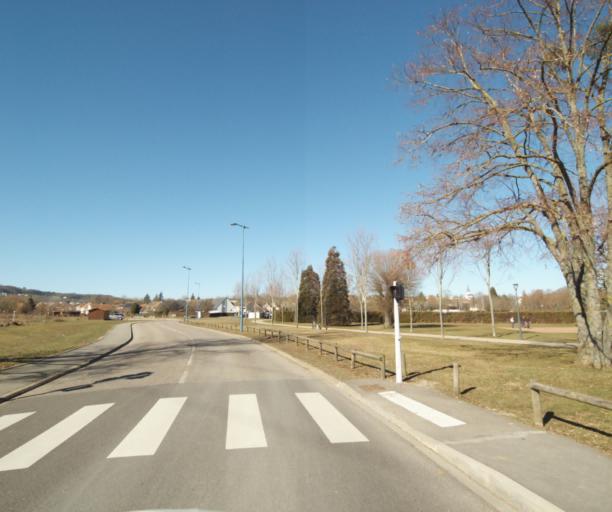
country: FR
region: Lorraine
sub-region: Departement de Meurthe-et-Moselle
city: Vandoeuvre-les-Nancy
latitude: 48.6479
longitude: 6.1961
